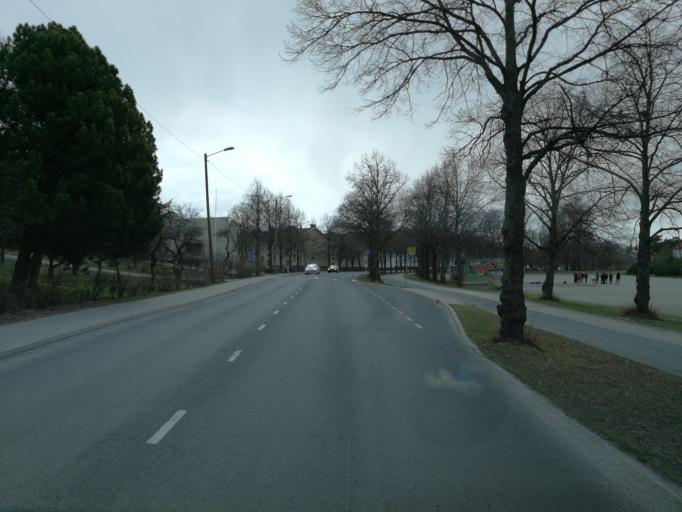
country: FI
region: Varsinais-Suomi
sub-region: Turku
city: Turku
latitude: 60.4398
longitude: 22.2709
